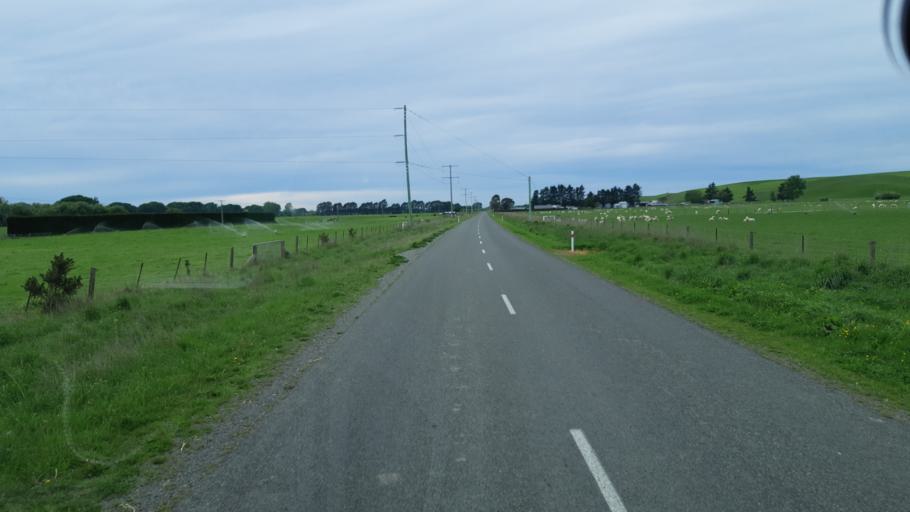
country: NZ
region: Canterbury
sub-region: Timaru District
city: Timaru
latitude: -44.4704
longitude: 171.1314
